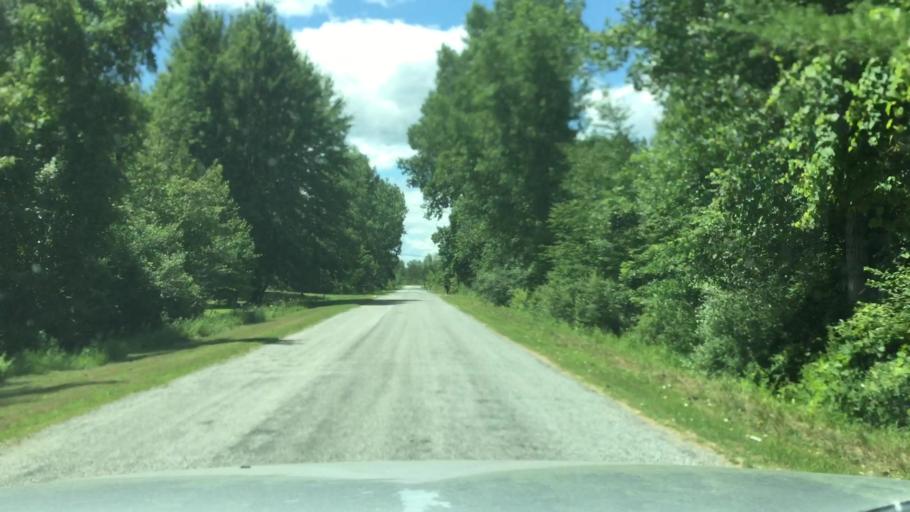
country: US
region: Michigan
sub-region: Saginaw County
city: Saint Charles
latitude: 43.3583
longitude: -84.1653
